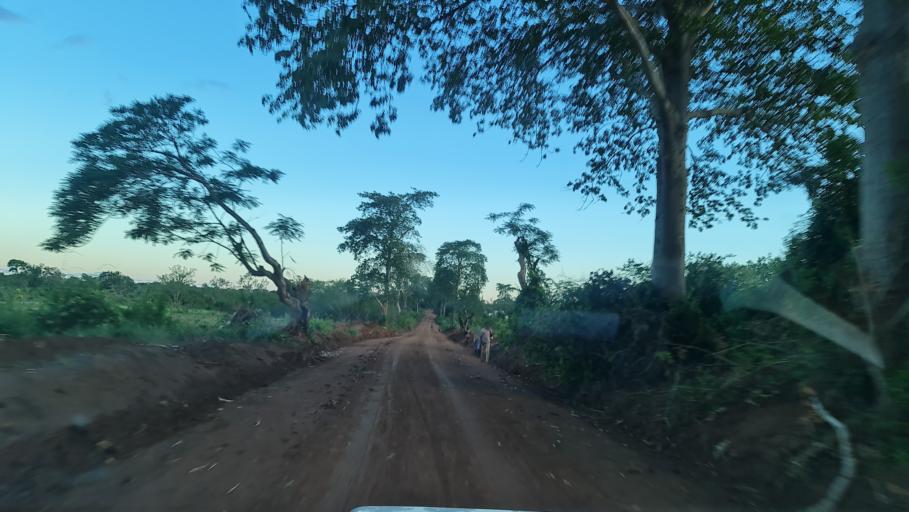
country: MZ
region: Nampula
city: Ilha de Mocambique
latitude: -14.9784
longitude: 40.0930
